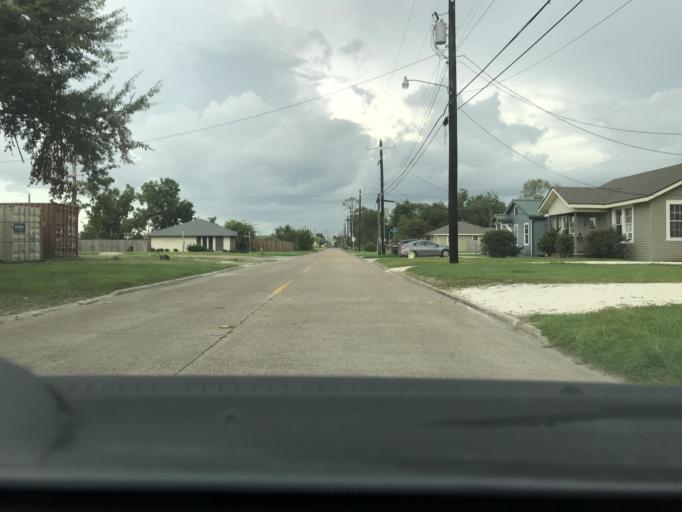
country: US
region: Louisiana
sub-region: Calcasieu Parish
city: Lake Charles
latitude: 30.2063
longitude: -93.2160
